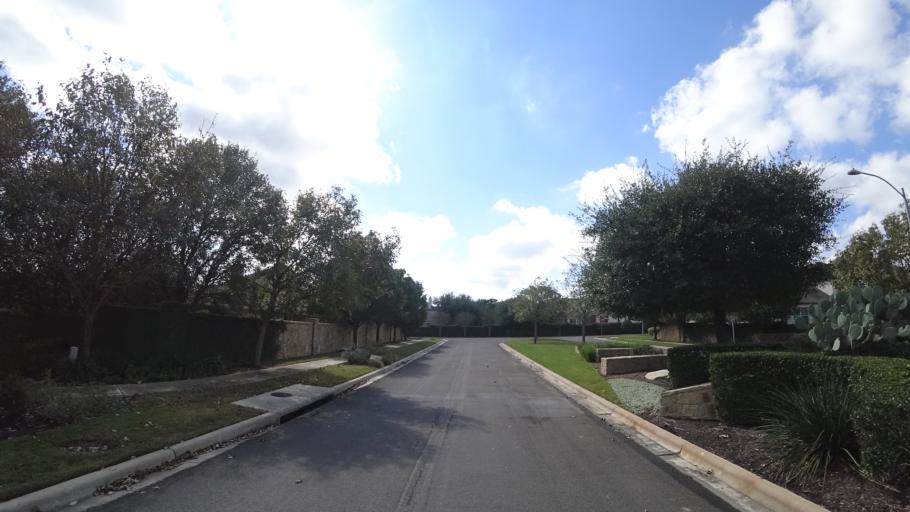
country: US
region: Texas
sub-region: Travis County
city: Barton Creek
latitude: 30.2572
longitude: -97.8822
